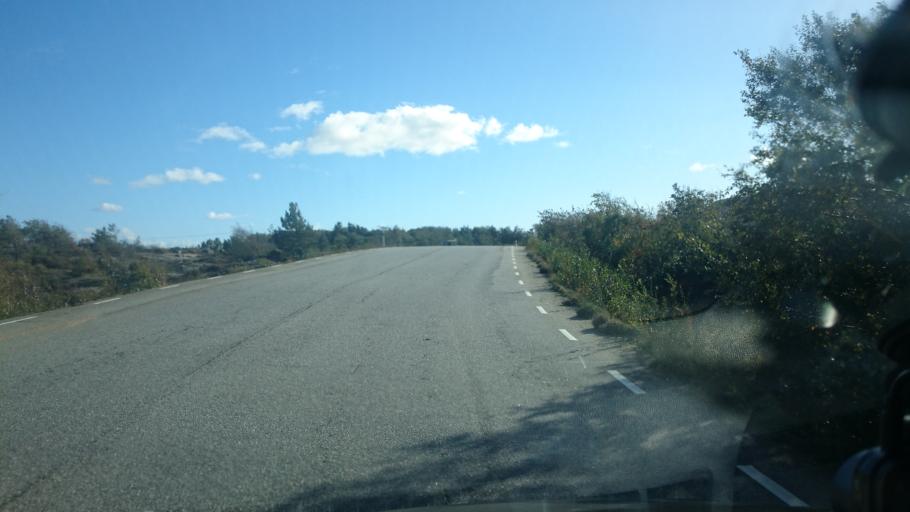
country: SE
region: Vaestra Goetaland
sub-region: Lysekils Kommun
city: Lysekil
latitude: 58.3244
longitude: 11.4162
